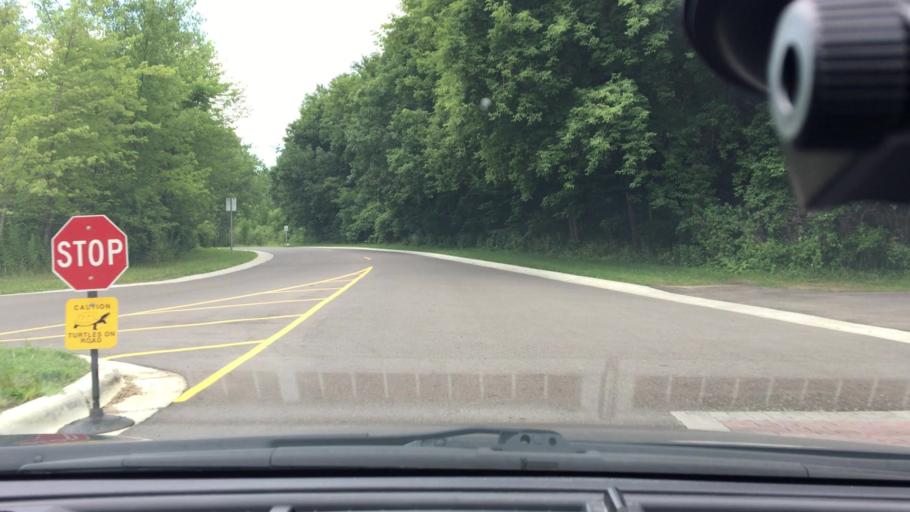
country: US
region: Minnesota
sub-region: Hennepin County
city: Plymouth
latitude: 45.0276
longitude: -93.4379
